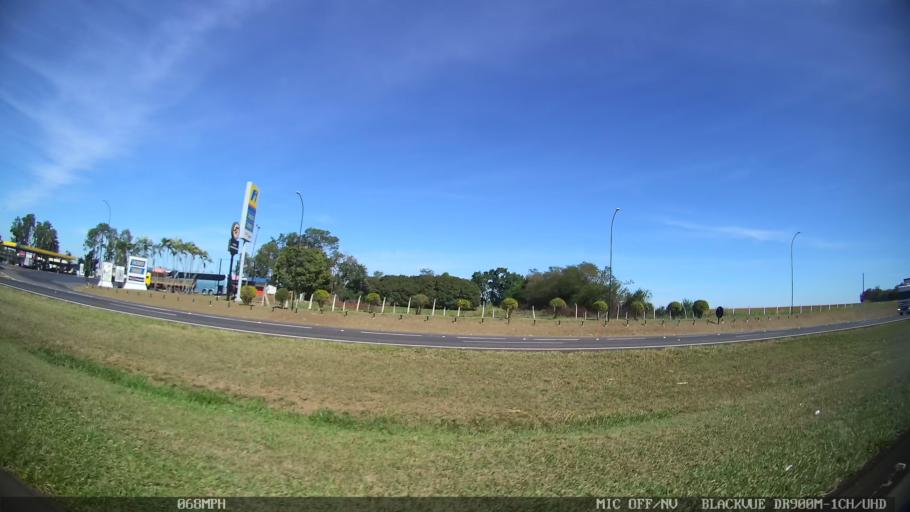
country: BR
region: Sao Paulo
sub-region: Santa Rita Do Passa Quatro
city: Santa Rita do Passa Quatro
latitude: -21.7783
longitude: -47.5354
